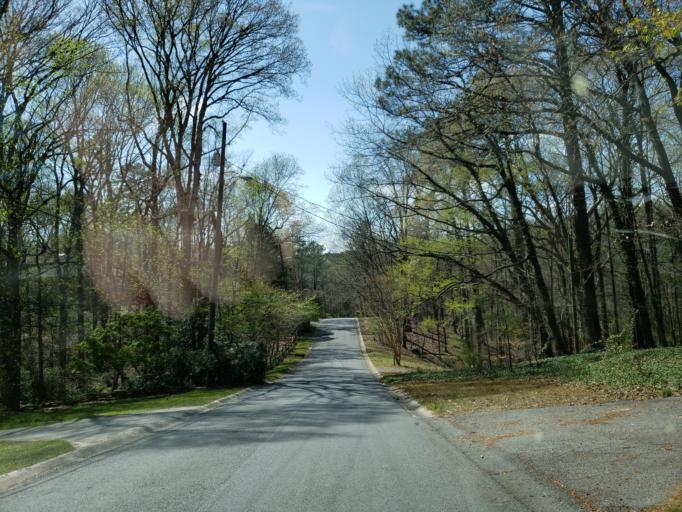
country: US
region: Georgia
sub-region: Cobb County
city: Marietta
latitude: 33.9639
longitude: -84.5700
